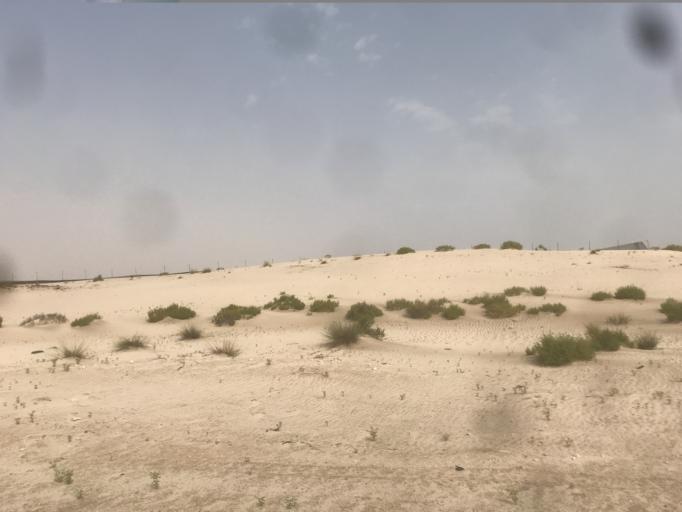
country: SA
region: Eastern Province
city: Abqaiq
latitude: 25.9070
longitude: 49.9993
